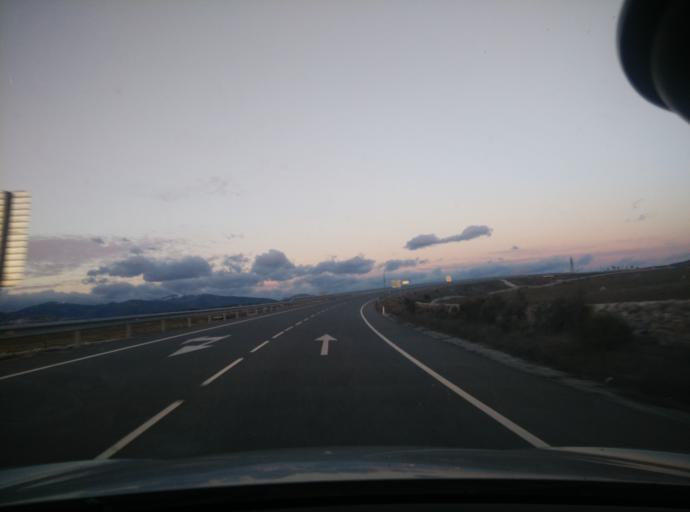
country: ES
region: Madrid
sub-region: Provincia de Madrid
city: Colmenar Viejo
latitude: 40.7247
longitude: -3.7899
